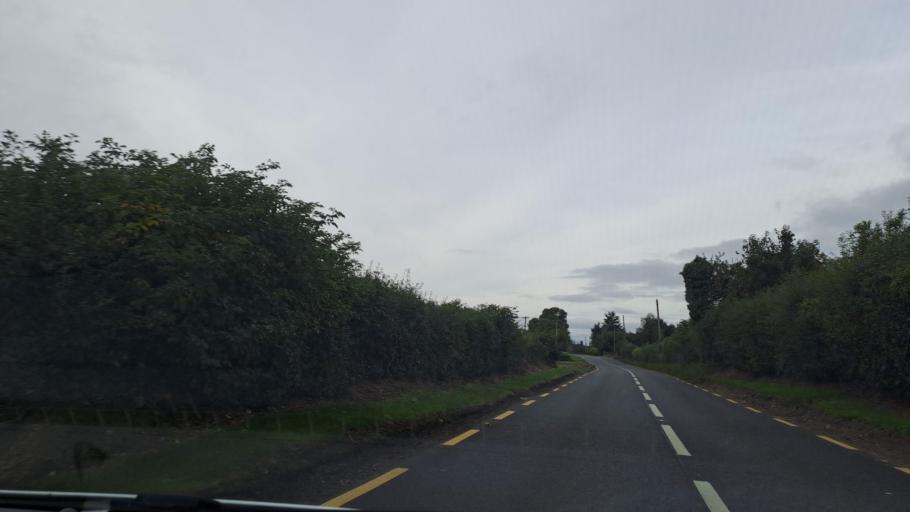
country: IE
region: Leinster
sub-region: Lu
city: Ardee
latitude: 53.8547
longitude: -6.5707
